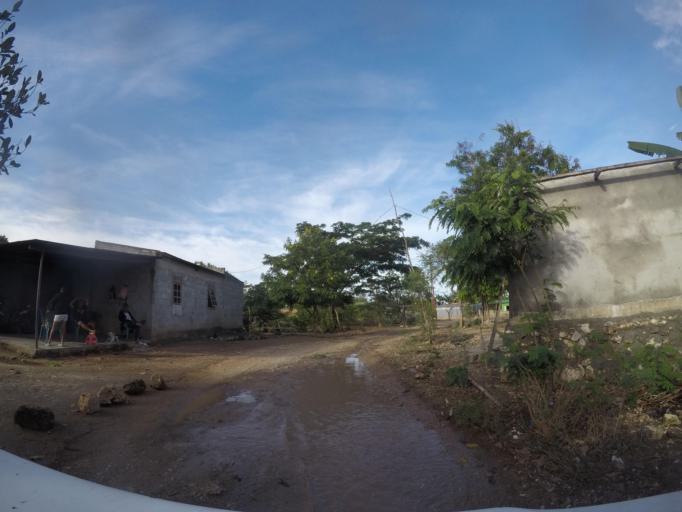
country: TL
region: Baucau
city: Baucau
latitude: -8.4867
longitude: 126.4543
